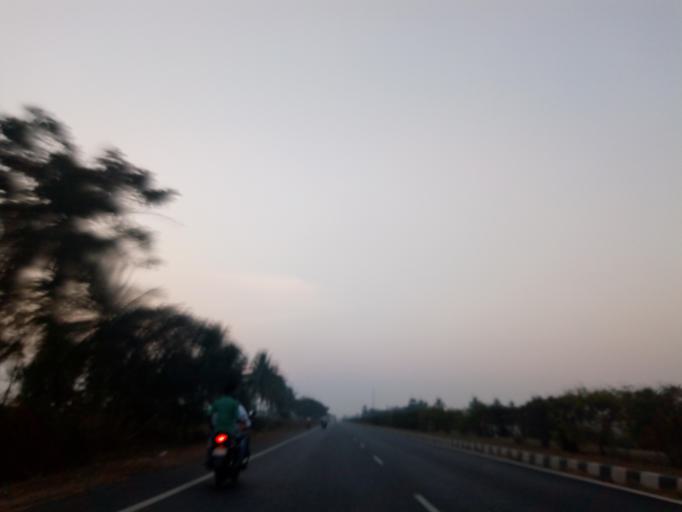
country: IN
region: Andhra Pradesh
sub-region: West Godavari
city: Tadepallegudem
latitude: 16.8241
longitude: 81.4438
